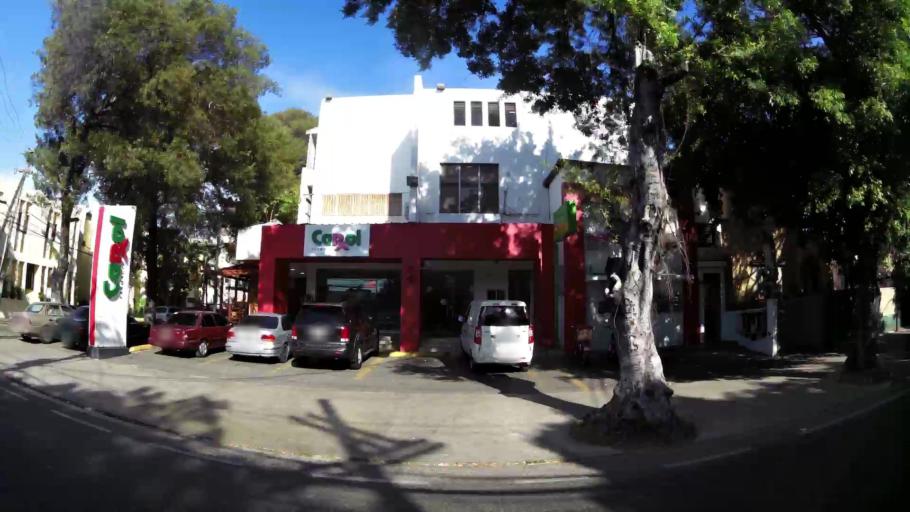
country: DO
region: Nacional
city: Ciudad Nueva
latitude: 18.4687
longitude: -69.8941
